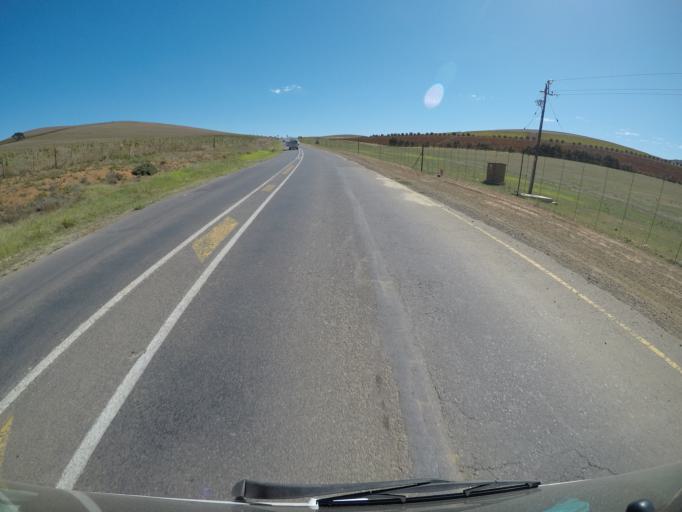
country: ZA
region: Western Cape
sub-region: City of Cape Town
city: Kraaifontein
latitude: -33.8019
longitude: 18.6182
